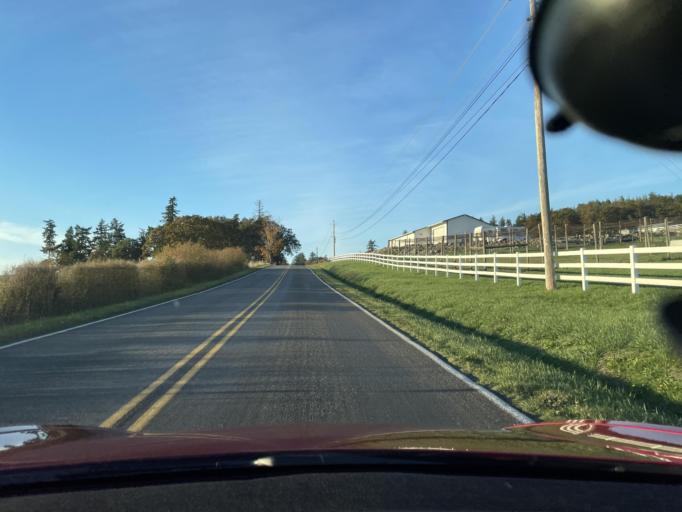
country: US
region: Washington
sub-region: San Juan County
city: Friday Harbor
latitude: 48.5740
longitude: -123.1392
